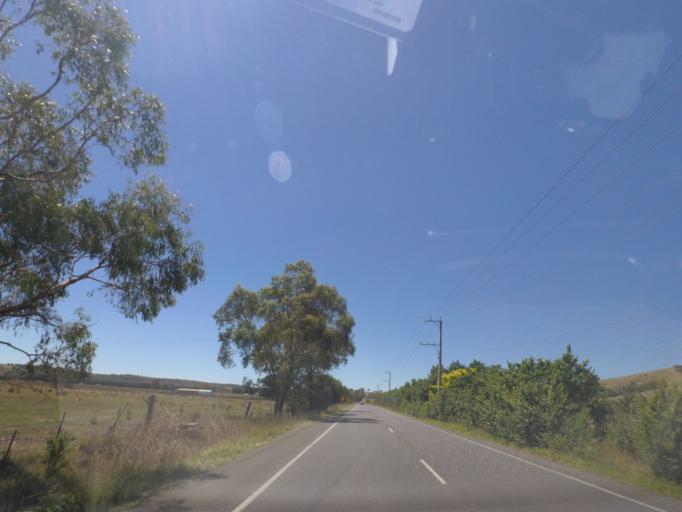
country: AU
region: Victoria
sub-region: Whittlesea
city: Whittlesea
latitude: -37.4203
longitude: 145.0228
